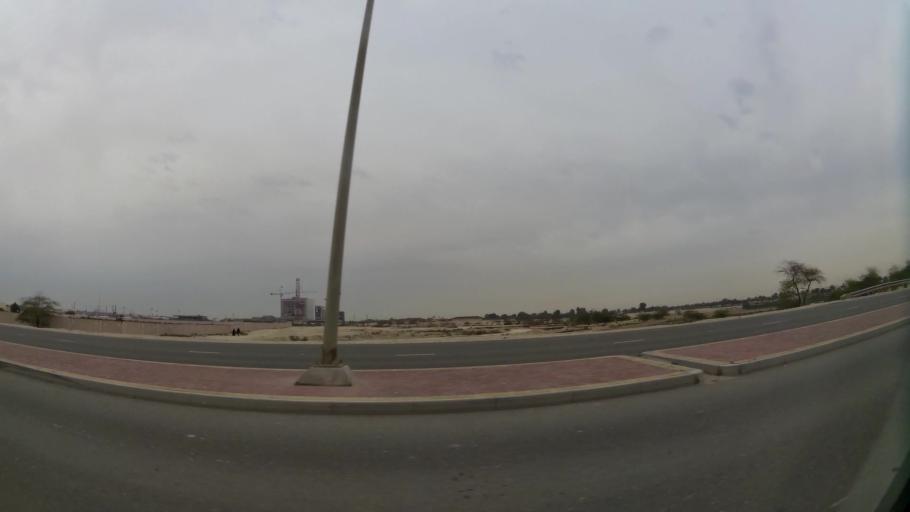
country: BH
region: Northern
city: Ar Rifa'
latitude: 26.0983
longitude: 50.5551
